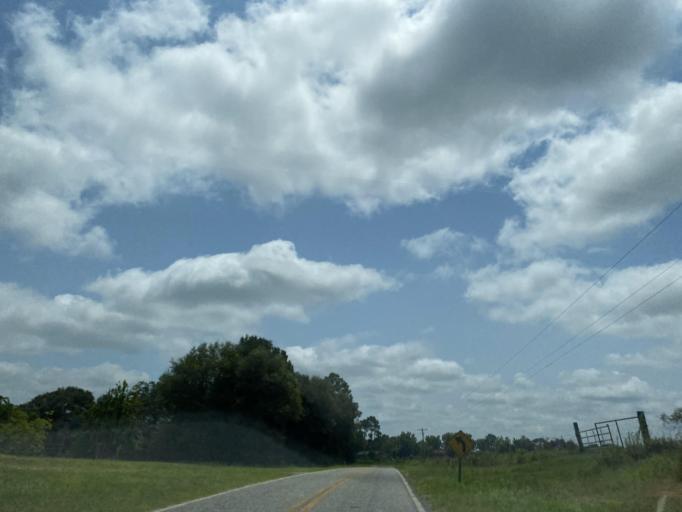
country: US
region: Georgia
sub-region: Wheeler County
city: Alamo
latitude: 32.0851
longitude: -82.7578
